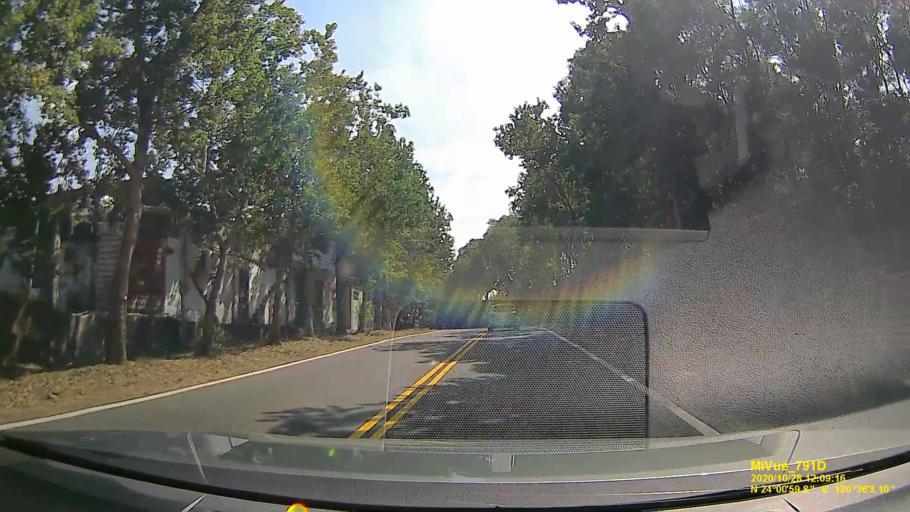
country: TW
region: Taiwan
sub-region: Changhua
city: Chang-hua
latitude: 24.0166
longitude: 120.6009
